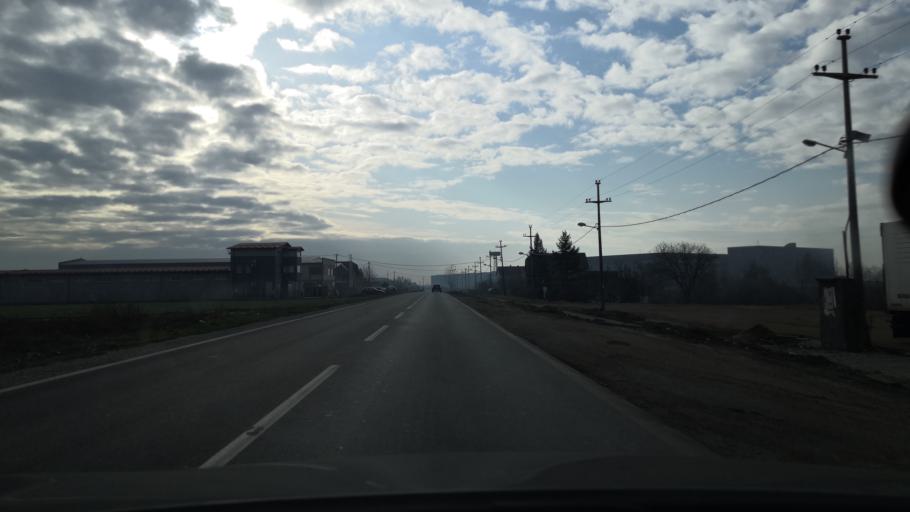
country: RS
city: Ugrinovci
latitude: 44.8579
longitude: 20.2051
